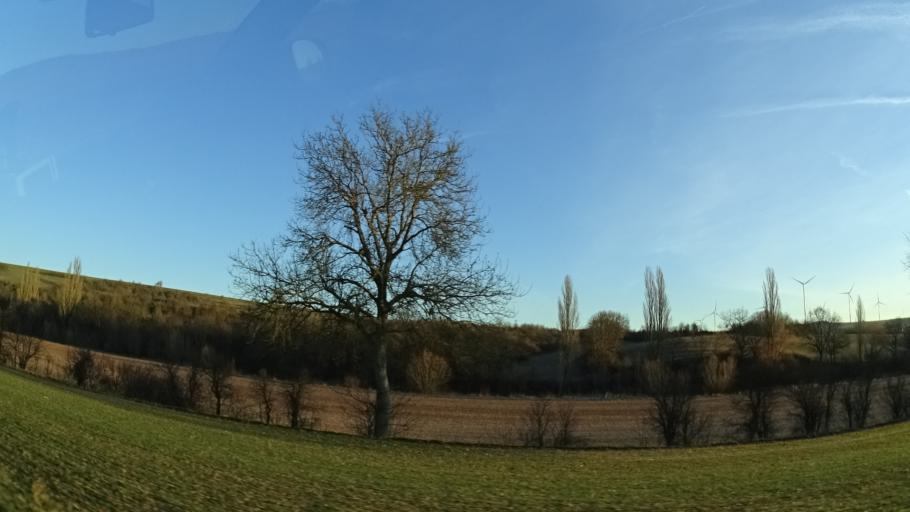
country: DE
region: Rheinland-Pfalz
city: Bolanden
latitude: 49.6361
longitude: 8.0211
